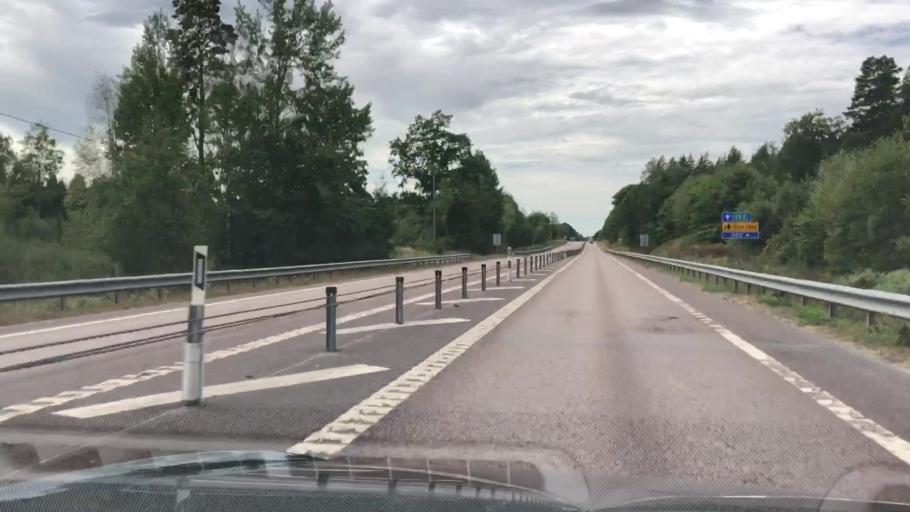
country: SE
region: Kalmar
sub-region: Torsas Kommun
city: Torsas
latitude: 56.2782
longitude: 15.9737
